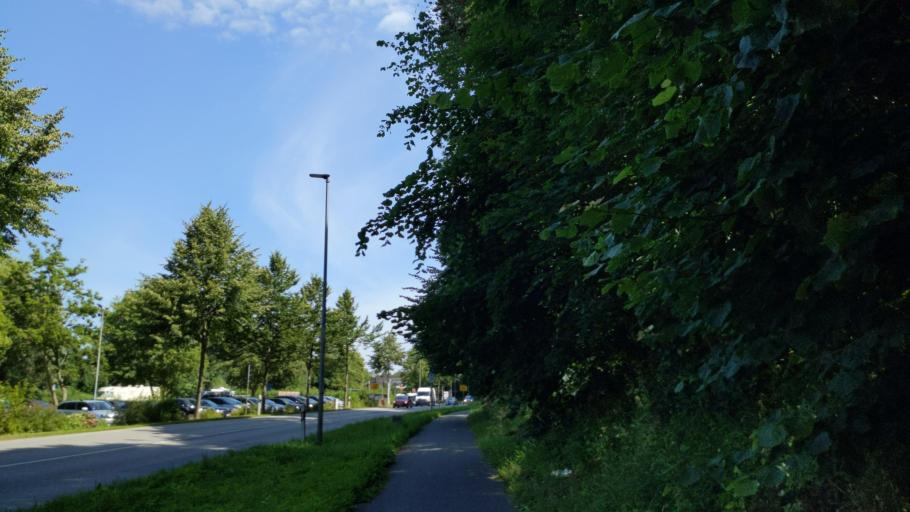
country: DE
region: Schleswig-Holstein
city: Ploen
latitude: 54.1521
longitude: 10.4035
